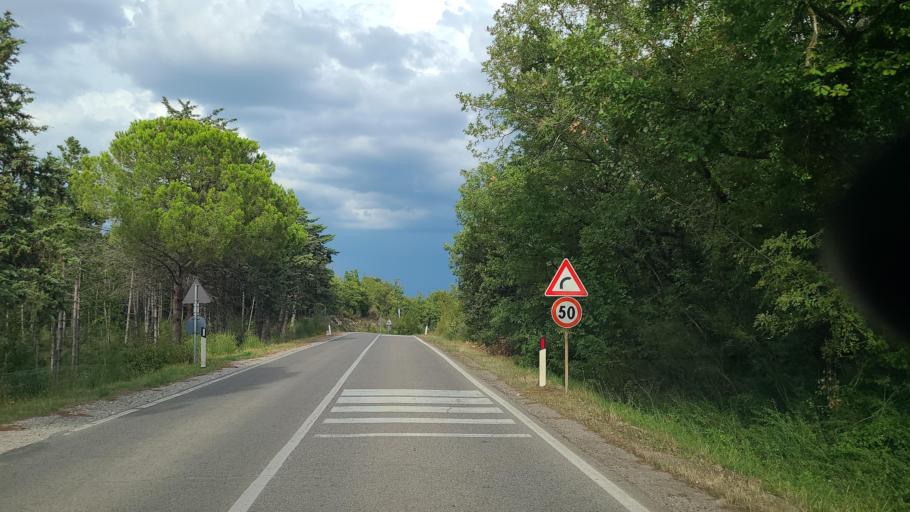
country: IT
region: Tuscany
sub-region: Provincia di Siena
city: San Gimignano
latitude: 43.4876
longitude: 10.9850
